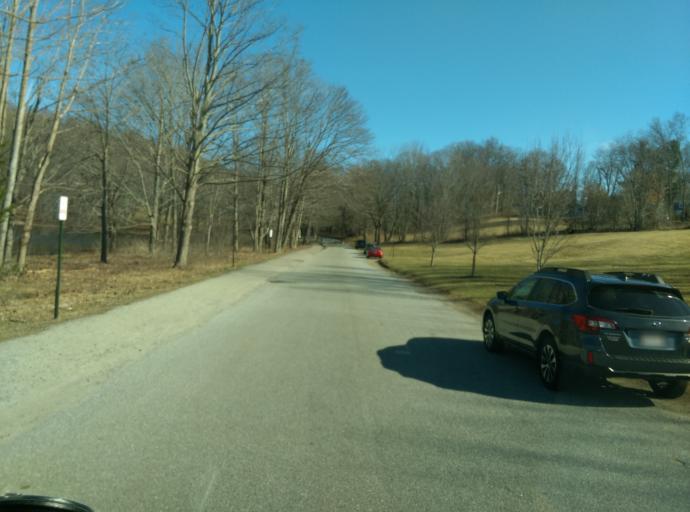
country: US
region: Massachusetts
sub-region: Essex County
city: Haverhill
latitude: 42.7901
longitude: -71.0683
